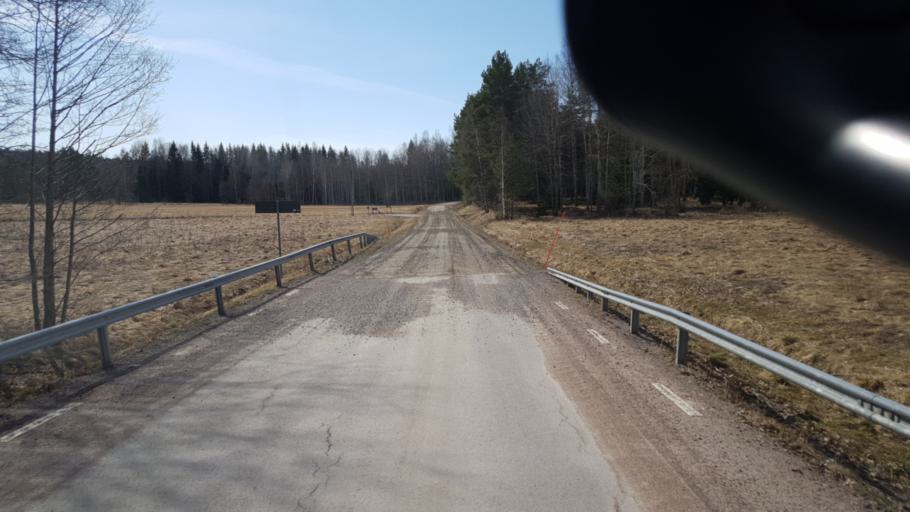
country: SE
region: Vaermland
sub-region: Arvika Kommun
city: Arvika
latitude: 59.5297
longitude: 12.7416
